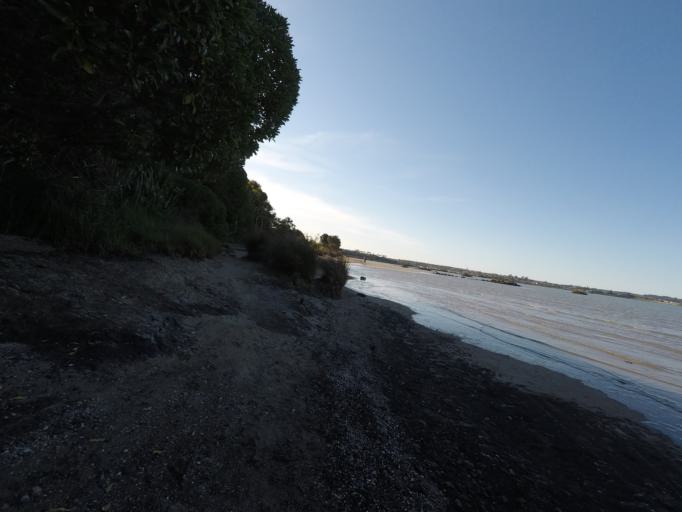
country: NZ
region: Auckland
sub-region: Auckland
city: Rosebank
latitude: -36.8302
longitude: 174.6589
